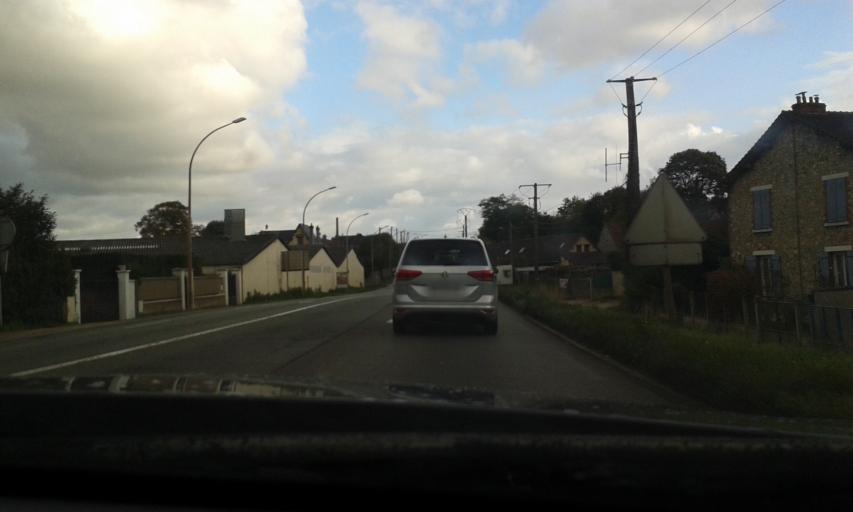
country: FR
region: Centre
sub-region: Departement d'Eure-et-Loir
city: Saint-Remy-sur-Avre
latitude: 48.7611
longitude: 1.2322
